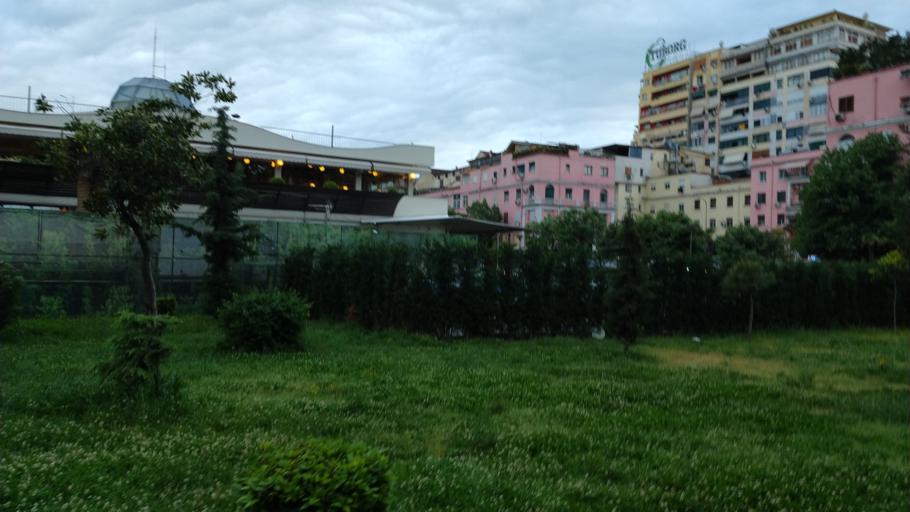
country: AL
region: Tirane
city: Tirana
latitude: 41.3253
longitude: 19.8176
